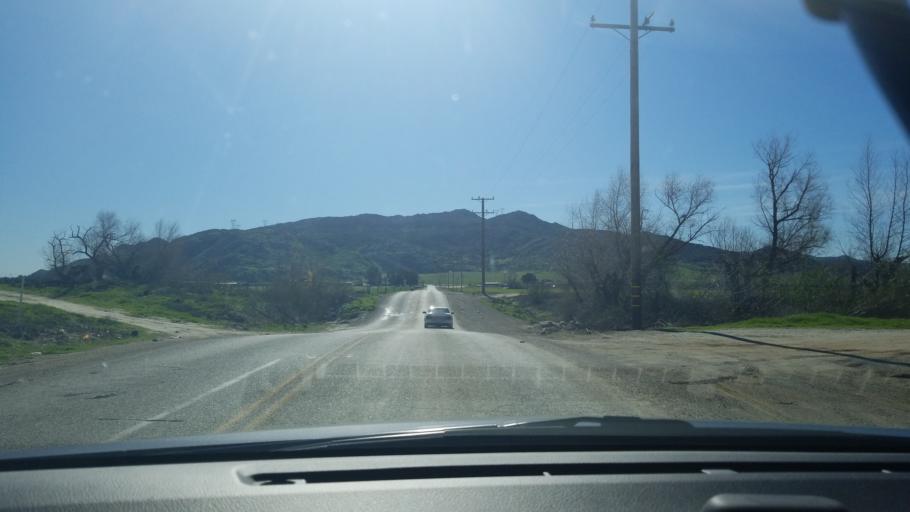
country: US
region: California
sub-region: Riverside County
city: Lakeview
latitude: 33.8536
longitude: -117.0684
